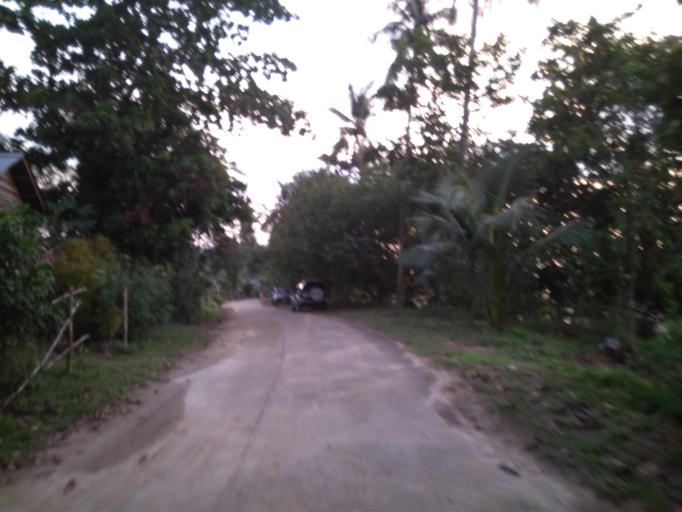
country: TH
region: Phangnga
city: Ko Yao
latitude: 8.1650
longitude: 98.6131
